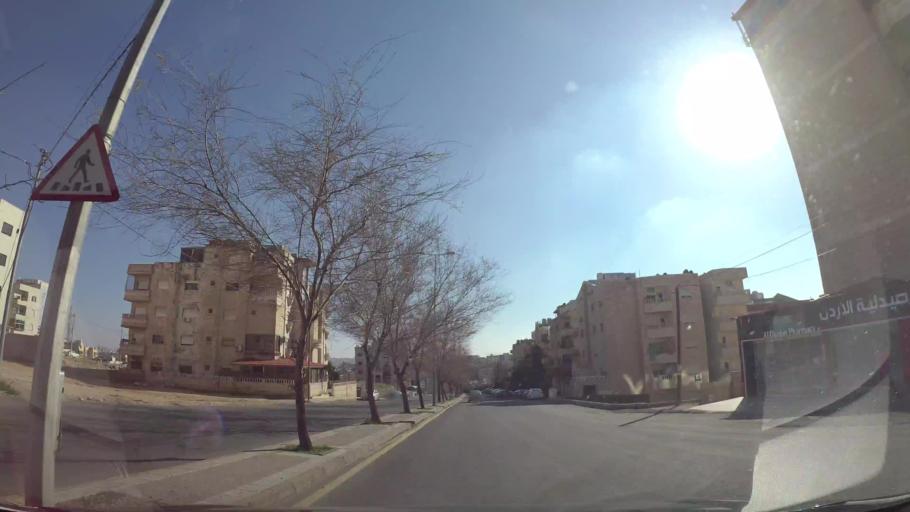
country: JO
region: Amman
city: Amman
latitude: 31.9788
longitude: 35.9395
